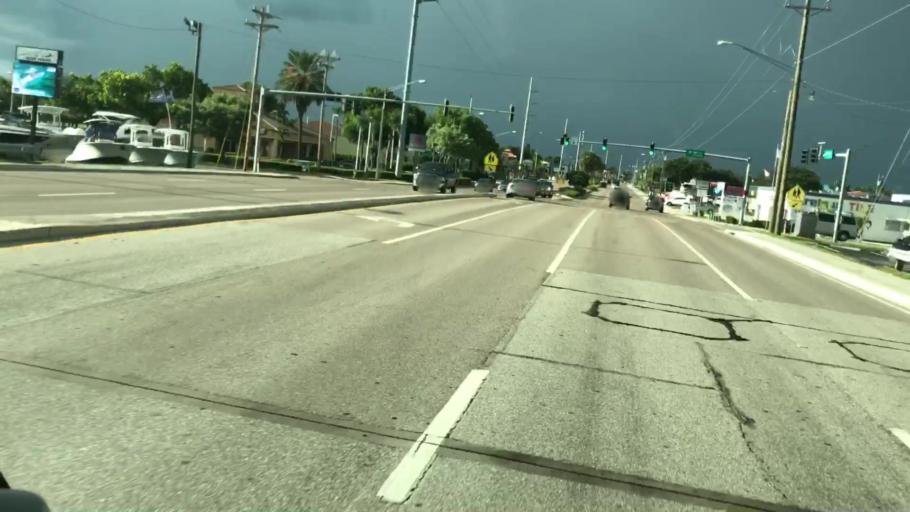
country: US
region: Florida
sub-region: Lee County
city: Cape Coral
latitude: 26.5662
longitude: -81.9438
